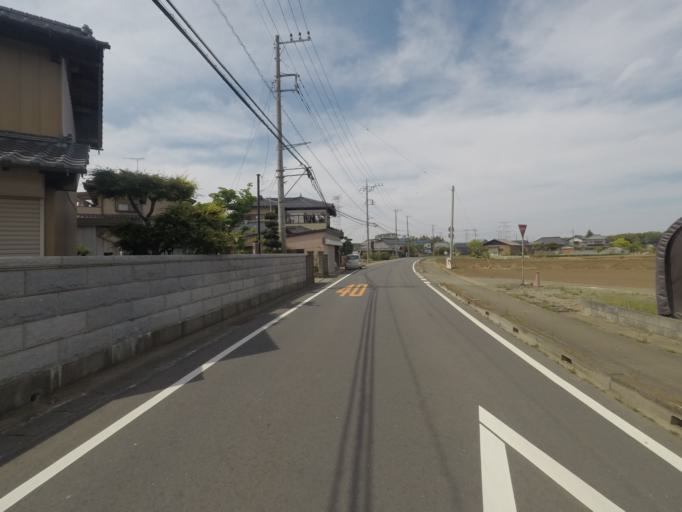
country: JP
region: Ibaraki
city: Ishige
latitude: 36.0782
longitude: 140.0374
